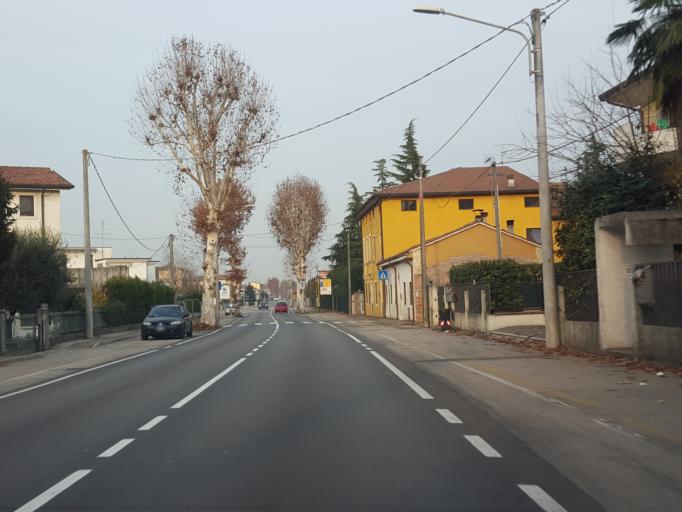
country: IT
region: Veneto
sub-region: Provincia di Vicenza
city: Creazzo
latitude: 45.5204
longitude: 11.5133
